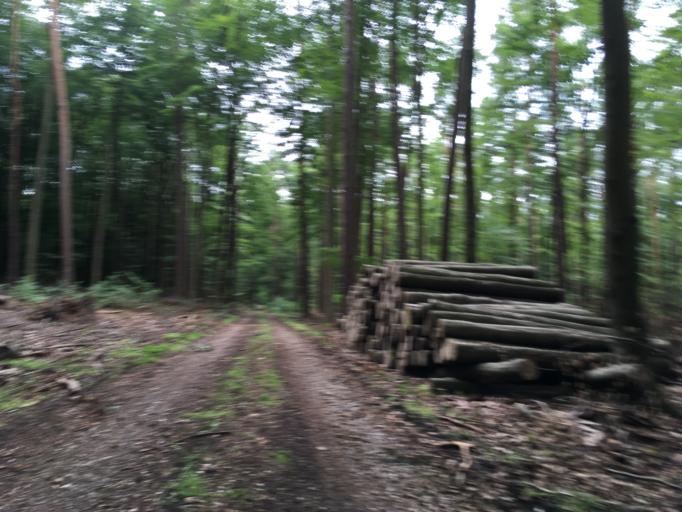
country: DE
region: Brandenburg
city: Wandlitz
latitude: 52.7446
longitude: 13.5257
